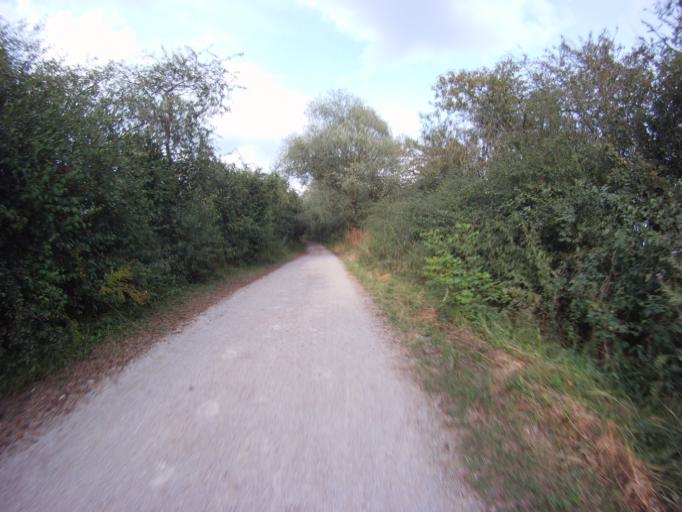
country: FR
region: Lorraine
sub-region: Departement de la Moselle
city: Mecleuves
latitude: 49.0732
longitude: 6.3294
